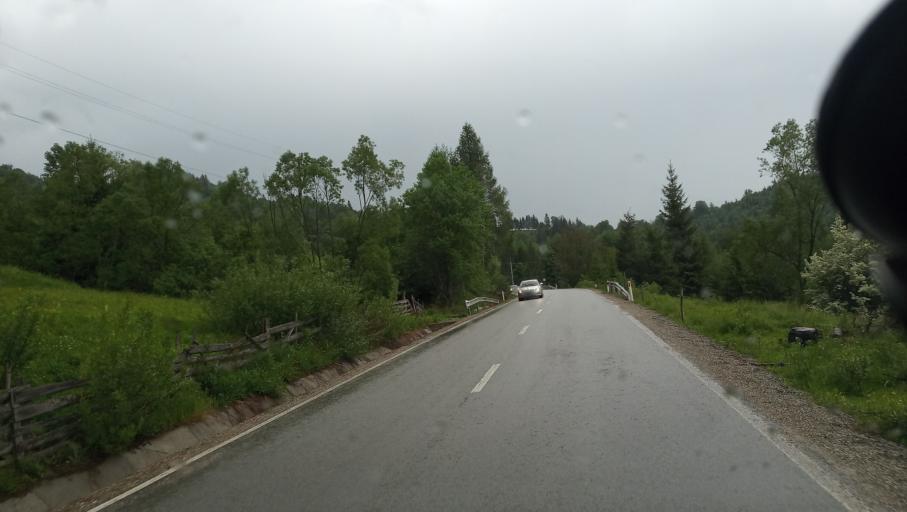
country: RO
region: Bistrita-Nasaud
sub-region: Comuna Tiha Bargaului
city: Tureac
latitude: 47.1941
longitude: 24.8836
